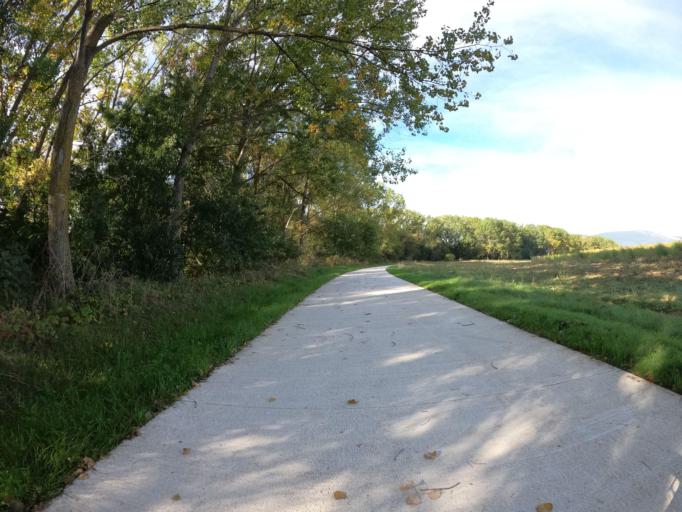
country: ES
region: Navarre
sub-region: Provincia de Navarra
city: Orkoien
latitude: 42.8105
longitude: -1.7308
